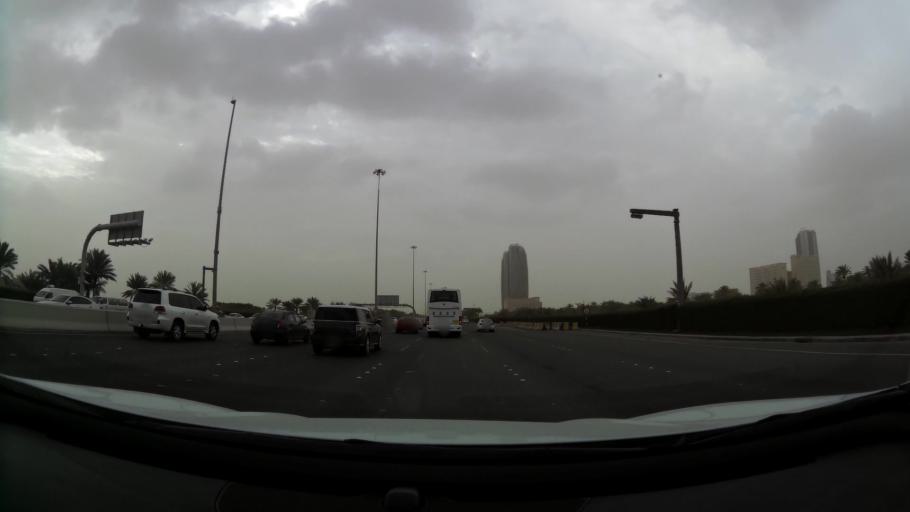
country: AE
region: Abu Dhabi
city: Abu Dhabi
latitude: 24.4636
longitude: 54.3976
